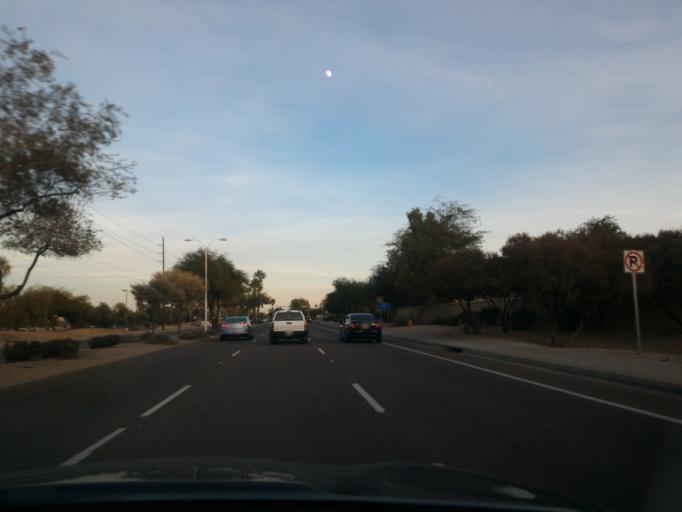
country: US
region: Arizona
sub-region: Maricopa County
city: Guadalupe
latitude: 33.3054
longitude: -111.9372
